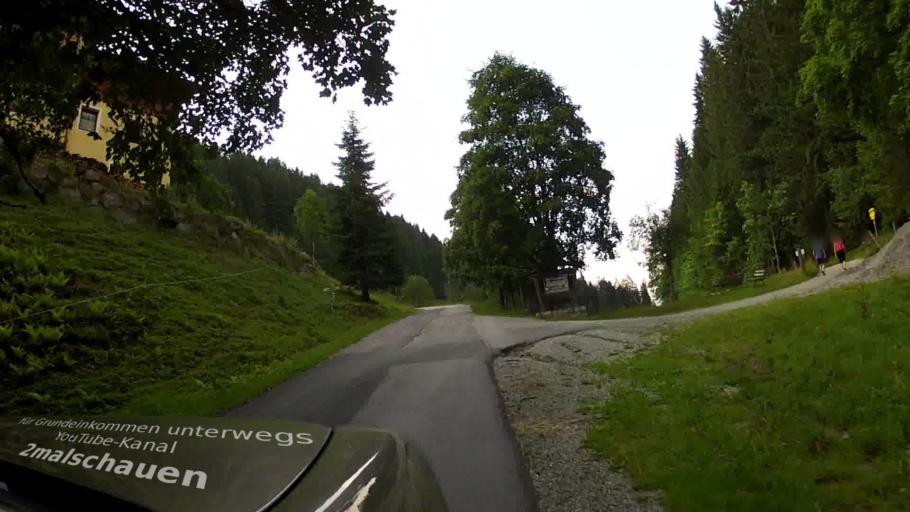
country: AT
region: Salzburg
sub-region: Politischer Bezirk Sankt Johann im Pongau
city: Eben im Pongau
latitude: 47.4382
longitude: 13.3821
